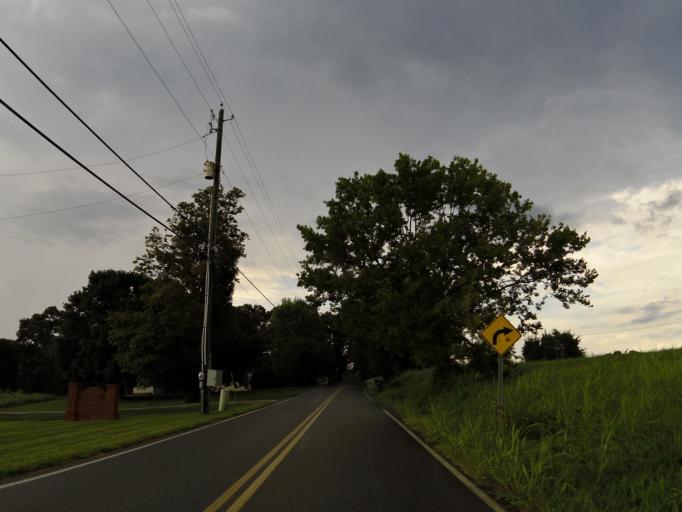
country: US
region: Tennessee
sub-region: Sevier County
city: Seymour
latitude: 35.8530
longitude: -83.7543
